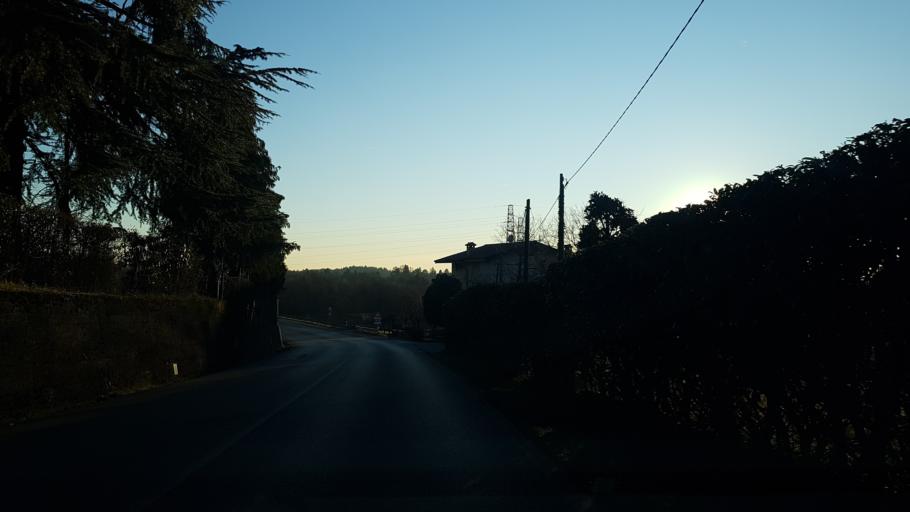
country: IT
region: Friuli Venezia Giulia
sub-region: Provincia di Udine
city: Tricesimo
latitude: 46.1806
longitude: 13.2194
